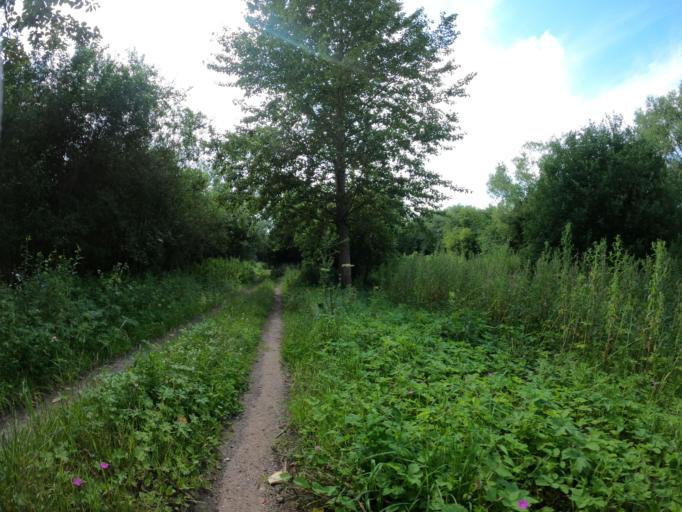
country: PL
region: West Pomeranian Voivodeship
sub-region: Powiat szczecinecki
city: Grzmiaca
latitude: 53.8319
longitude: 16.4444
